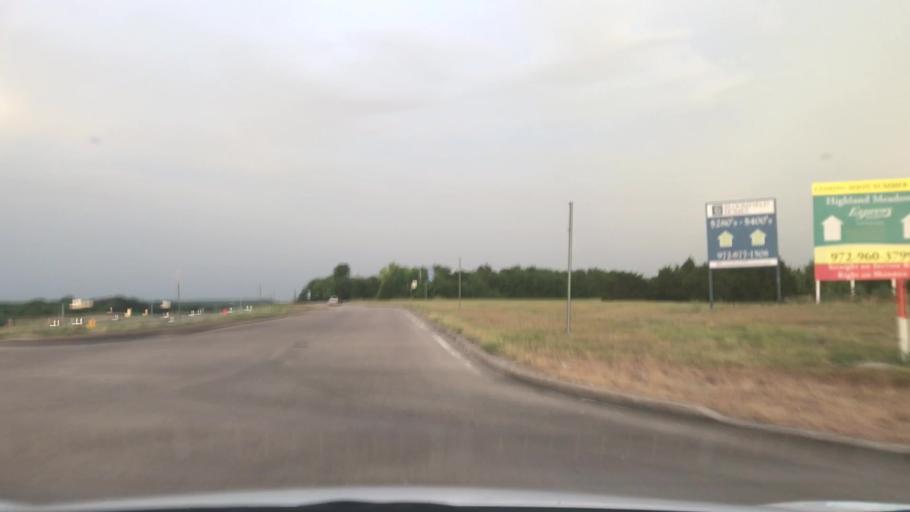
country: US
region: Texas
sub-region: Dallas County
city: Balch Springs
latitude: 32.7030
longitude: -96.5695
